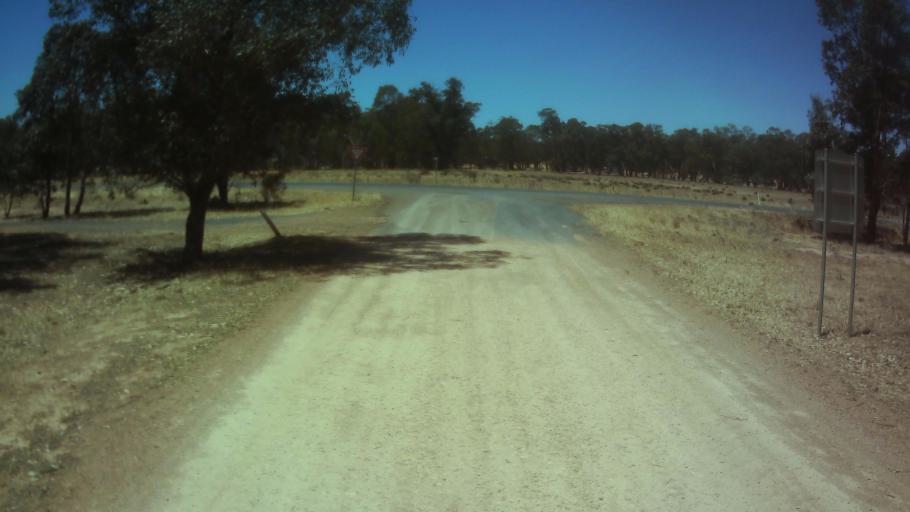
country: AU
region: New South Wales
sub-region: Weddin
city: Grenfell
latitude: -33.7562
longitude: 148.2177
